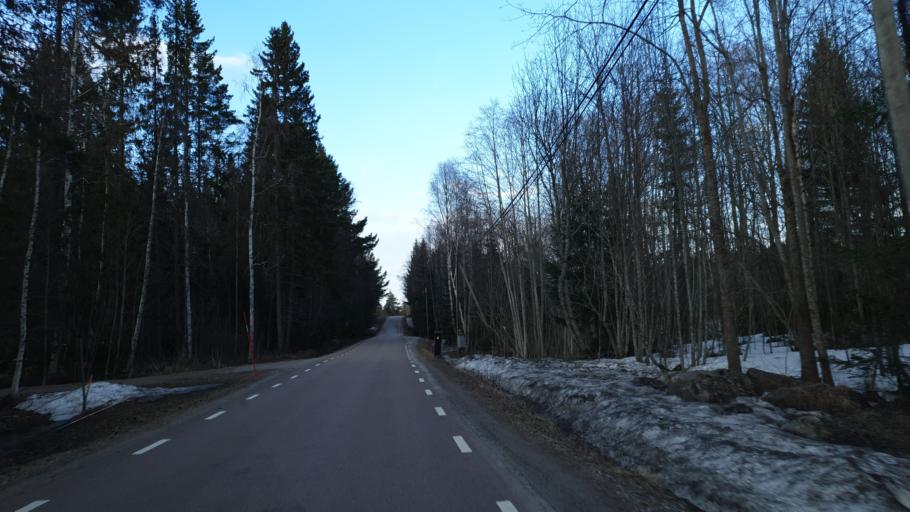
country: SE
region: Vaesternorrland
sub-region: Sundsvalls Kommun
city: Njurundabommen
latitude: 62.2352
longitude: 17.5135
